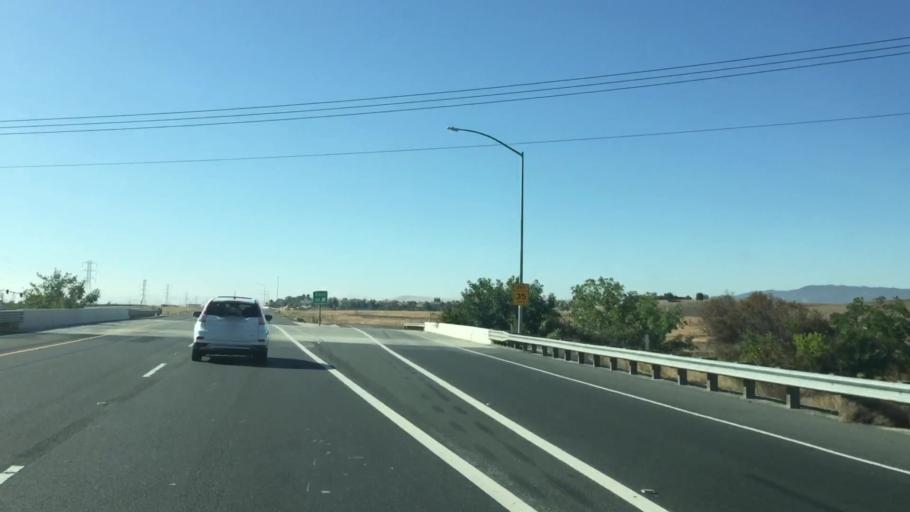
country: US
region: California
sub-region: Contra Costa County
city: Brentwood
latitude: 37.9474
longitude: -121.7438
